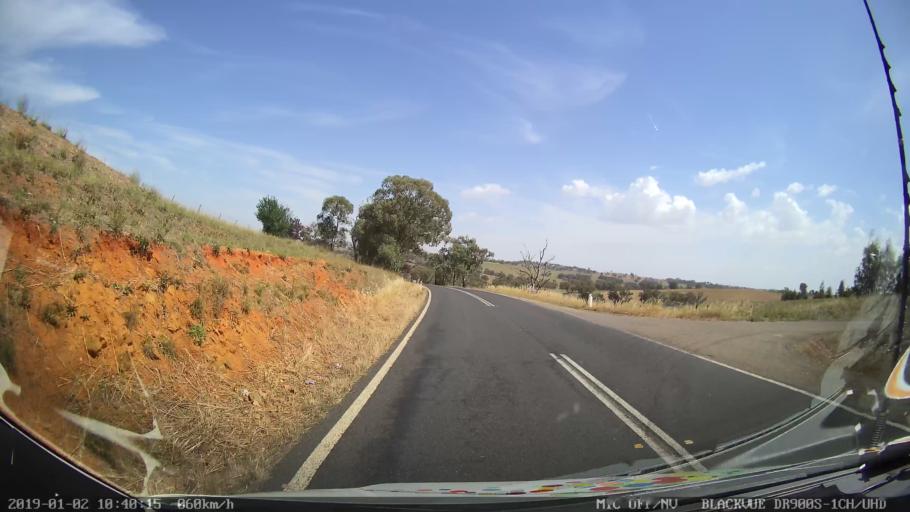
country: AU
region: New South Wales
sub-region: Cootamundra
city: Cootamundra
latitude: -34.8034
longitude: 148.3170
